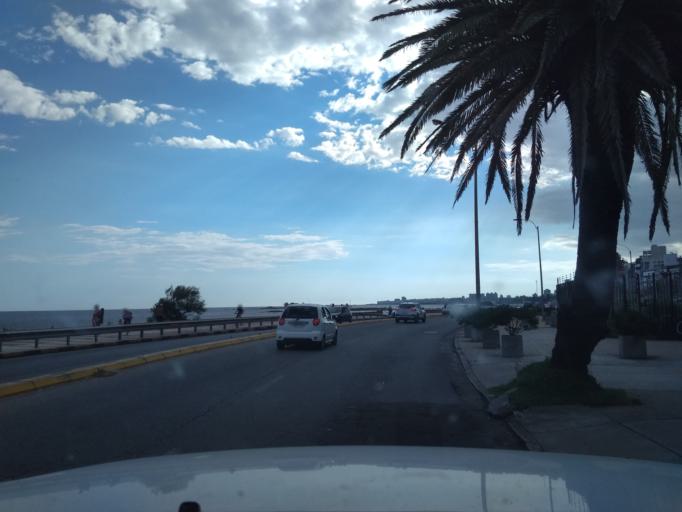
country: UY
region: Canelones
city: Paso de Carrasco
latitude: -34.8966
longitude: -56.0960
